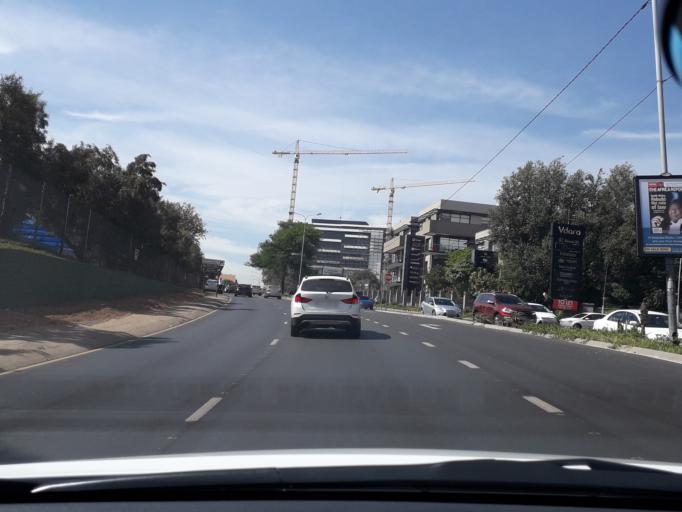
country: ZA
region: Gauteng
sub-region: City of Johannesburg Metropolitan Municipality
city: Johannesburg
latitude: -26.1179
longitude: 28.0463
